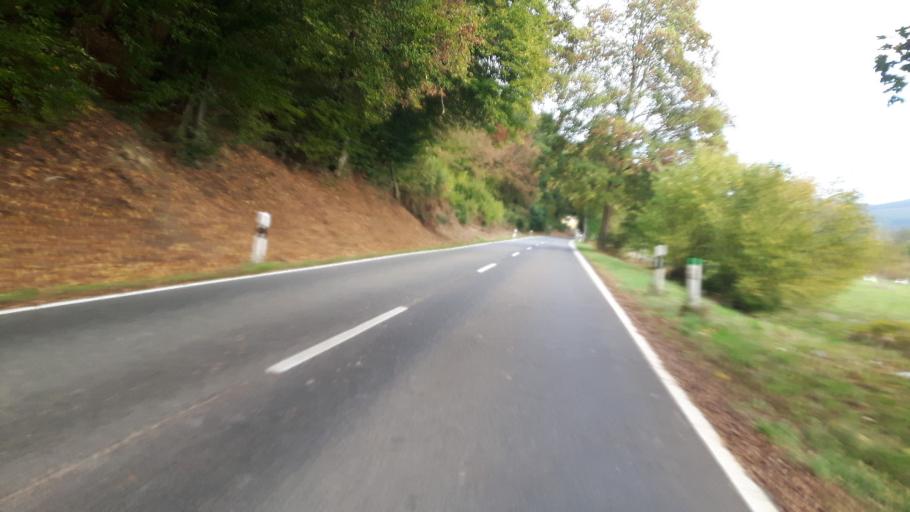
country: DE
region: North Rhine-Westphalia
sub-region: Regierungsbezirk Koln
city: Eitorf
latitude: 50.7700
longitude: 7.4905
